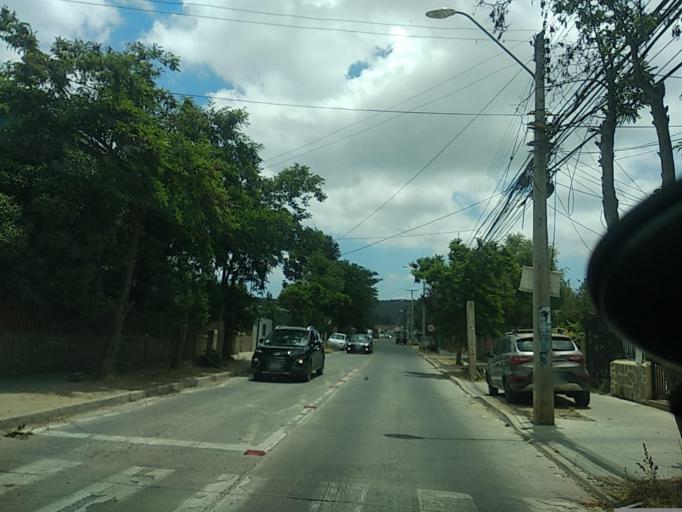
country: CL
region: Valparaiso
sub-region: Provincia de Marga Marga
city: Villa Alemana
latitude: -33.0361
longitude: -71.4056
